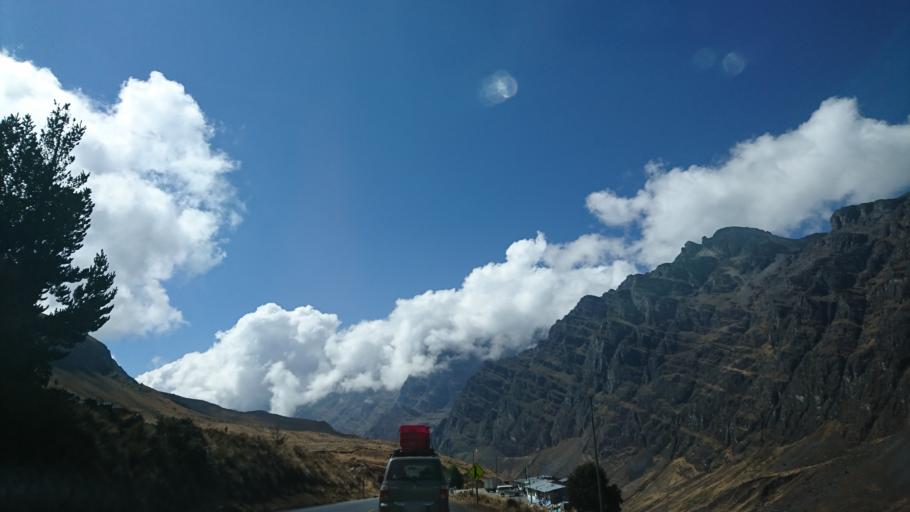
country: BO
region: La Paz
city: La Paz
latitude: -16.3270
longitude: -67.9897
